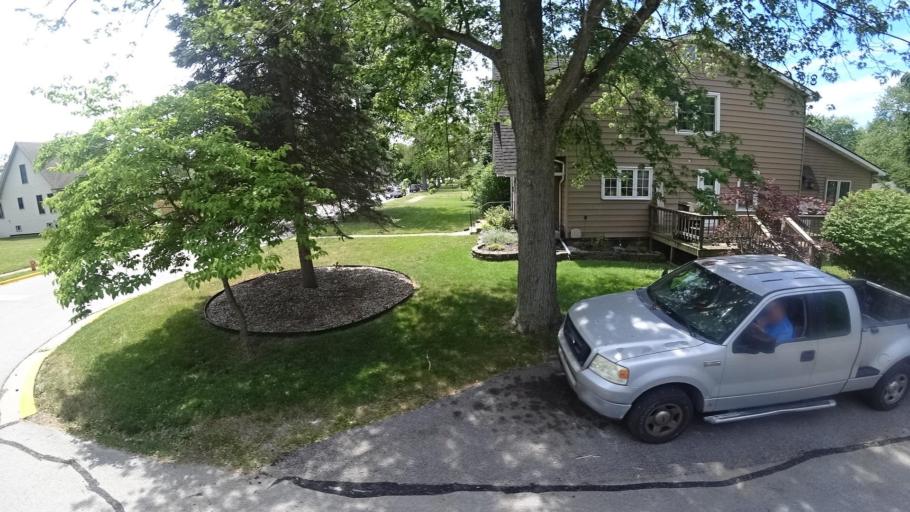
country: US
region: Indiana
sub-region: Porter County
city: Porter
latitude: 41.6196
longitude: -87.0733
